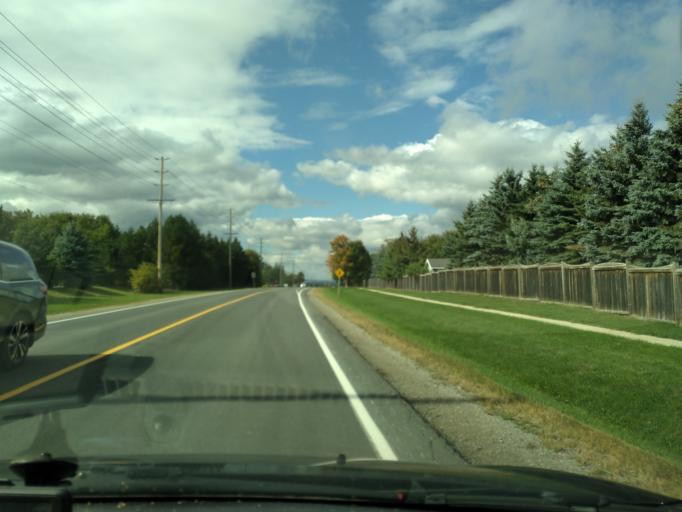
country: CA
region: Ontario
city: Innisfil
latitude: 44.2687
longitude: -79.7313
